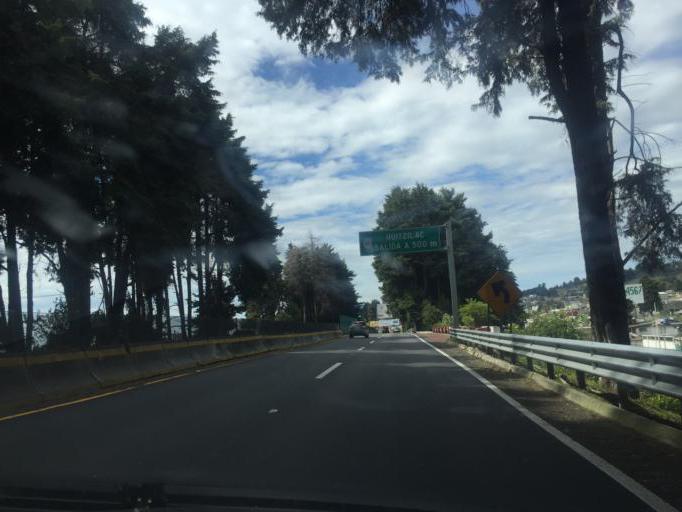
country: MX
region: Morelos
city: Tres Marias
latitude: 19.0588
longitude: -99.2396
